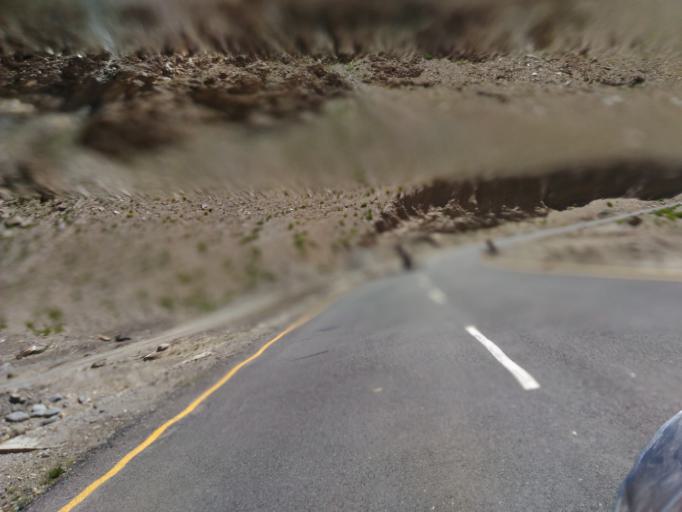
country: IN
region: Kashmir
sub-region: Ladakh
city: Leh
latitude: 33.5817
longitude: 77.7487
